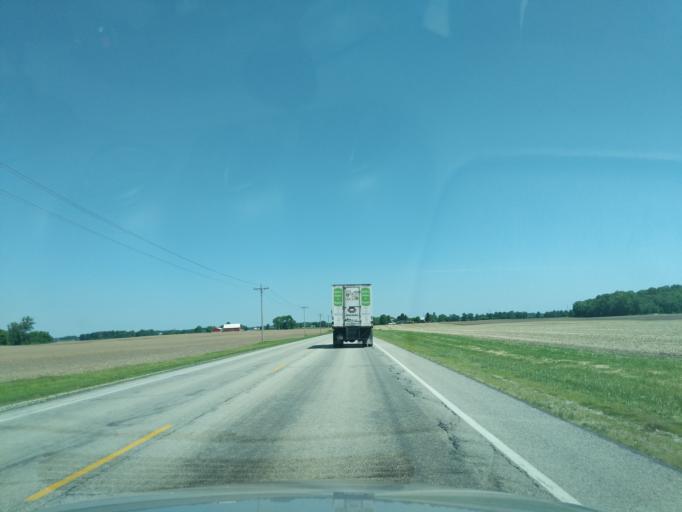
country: US
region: Indiana
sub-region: Huntington County
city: Roanoke
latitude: 41.0354
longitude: -85.4706
